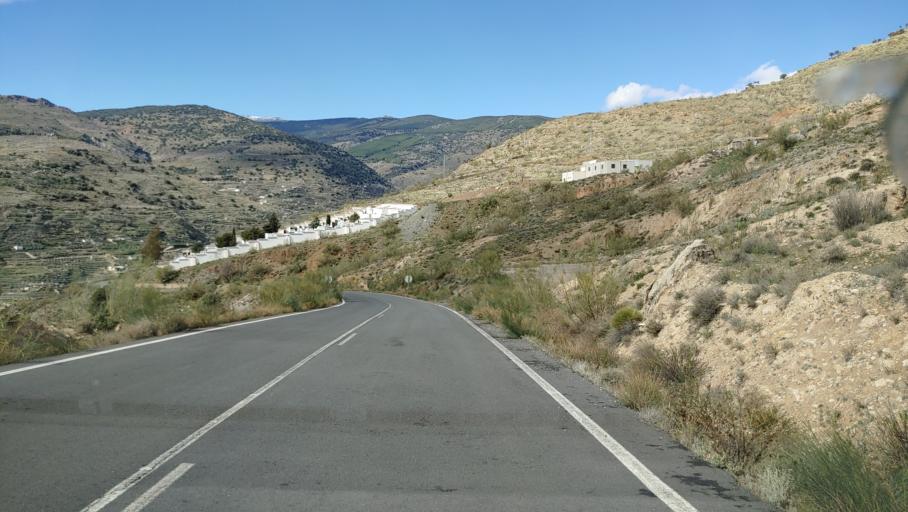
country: ES
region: Andalusia
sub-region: Provincia de Almeria
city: Ohanes
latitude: 37.0323
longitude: -2.7385
